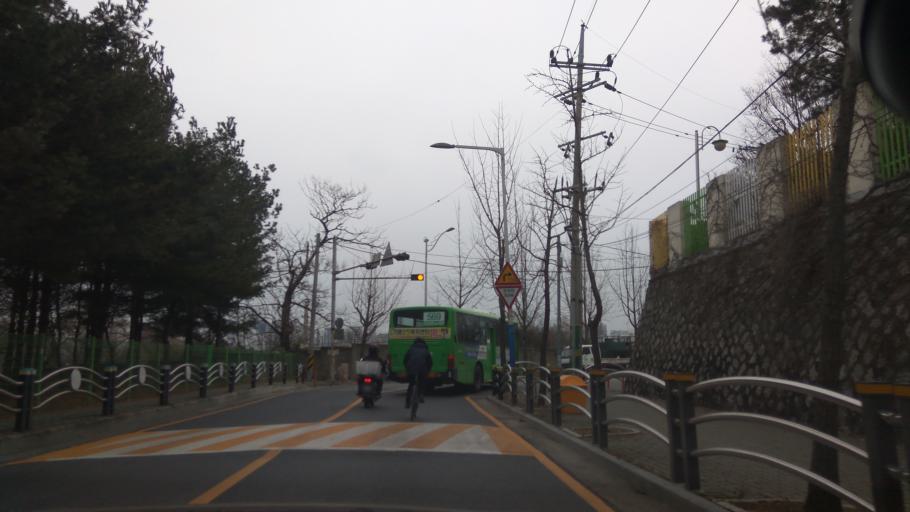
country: KR
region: Incheon
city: Incheon
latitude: 37.4940
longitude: 126.7095
